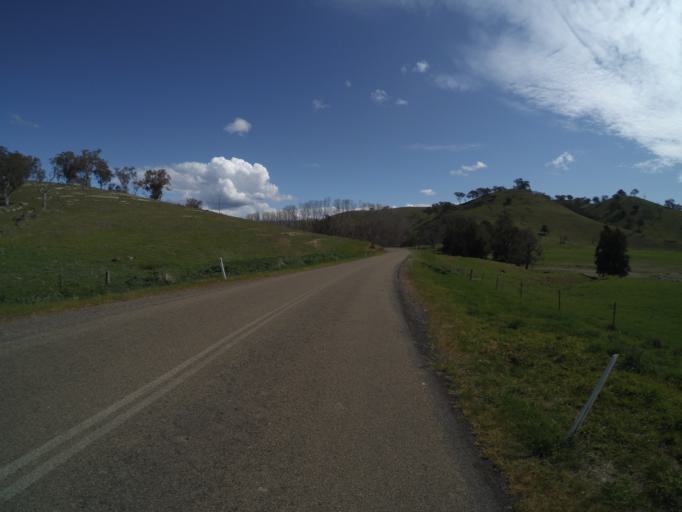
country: AU
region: New South Wales
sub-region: Yass Valley
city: Yass
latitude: -35.0220
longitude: 148.8375
